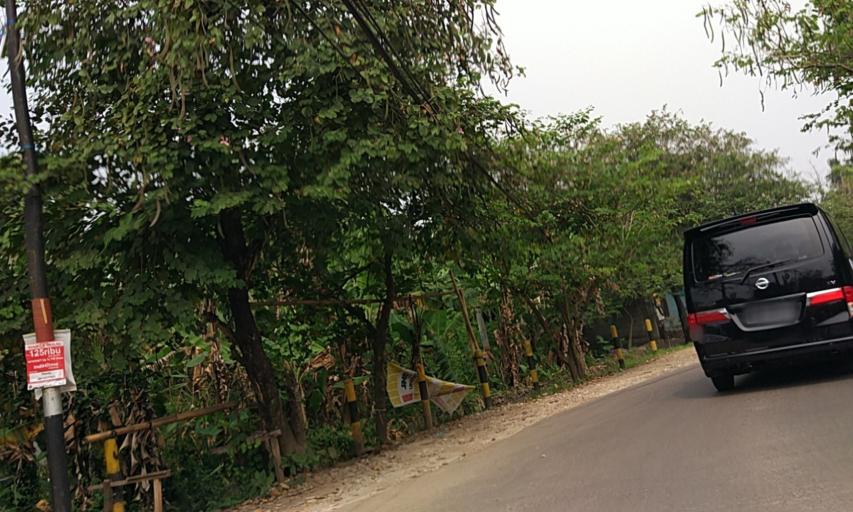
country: ID
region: West Java
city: Bandung
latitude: -6.9068
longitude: 107.6573
